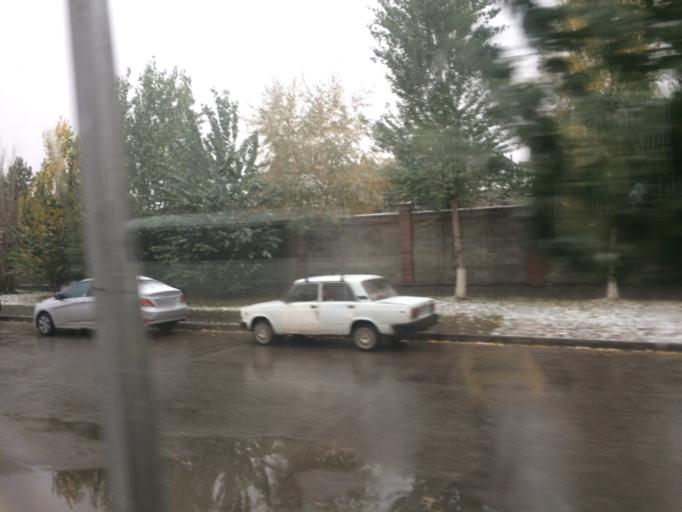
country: KZ
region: Astana Qalasy
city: Astana
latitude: 51.1424
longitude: 71.4450
